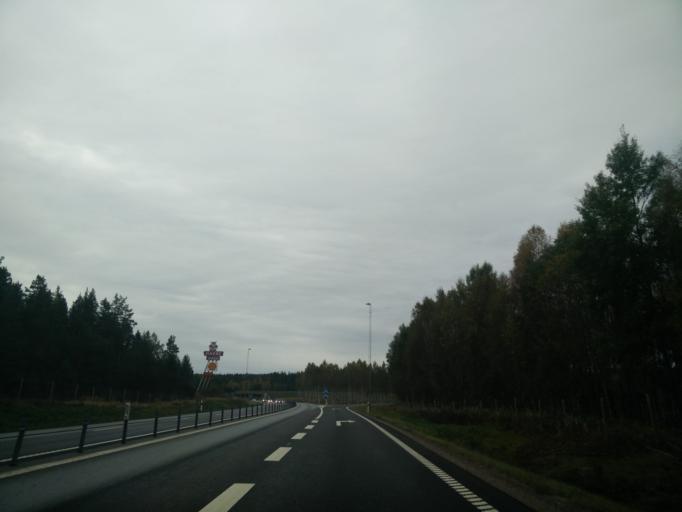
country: SE
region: Gaevleborg
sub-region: Gavle Kommun
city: Norrsundet
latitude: 60.9059
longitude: 17.0150
